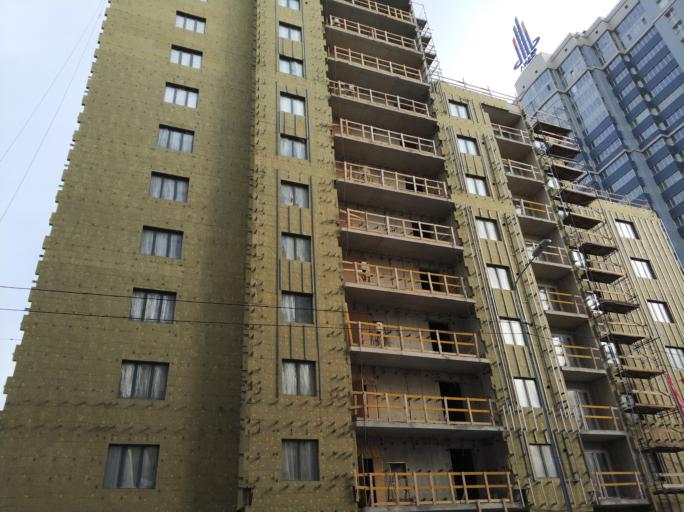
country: RU
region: St.-Petersburg
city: Saint Petersburg
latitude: 59.9043
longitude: 30.3230
